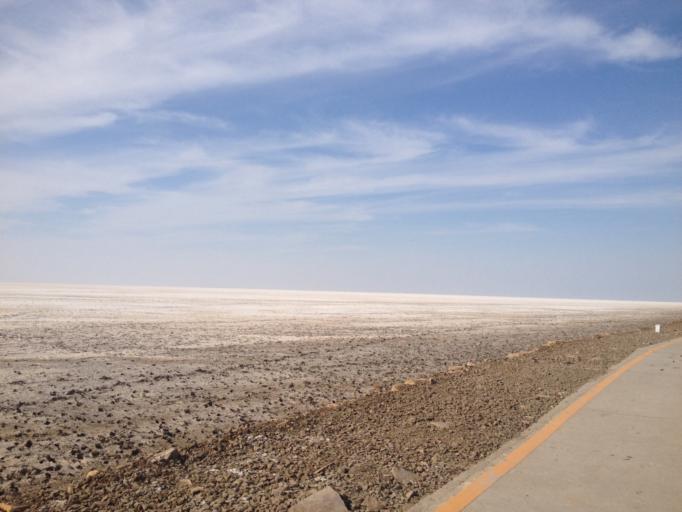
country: IN
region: Gujarat
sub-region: Kachchh
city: Bhuj
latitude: 23.8310
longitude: 69.5216
